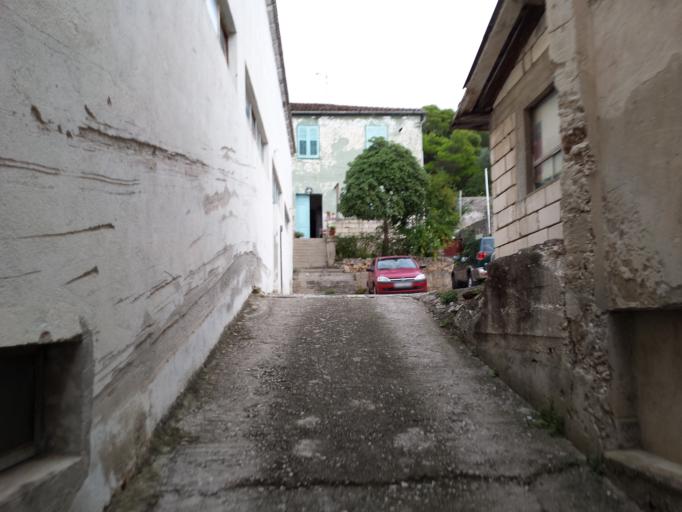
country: HR
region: Sibensko-Kniniska
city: Rogoznica
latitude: 43.5243
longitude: 15.9686
